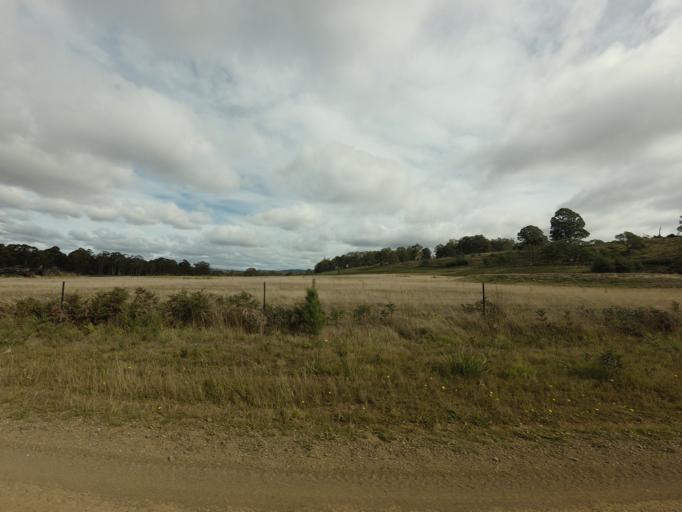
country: AU
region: Tasmania
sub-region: Brighton
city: Bridgewater
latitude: -42.4192
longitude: 147.4189
